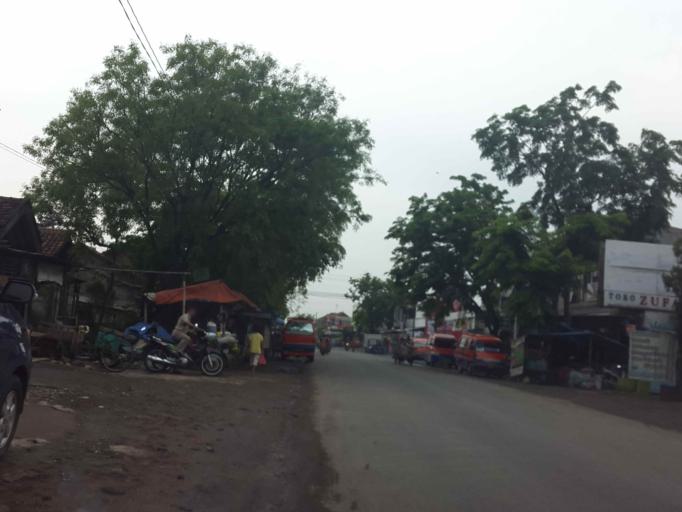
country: ID
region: Central Java
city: Semarang
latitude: -6.9524
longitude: 110.4808
